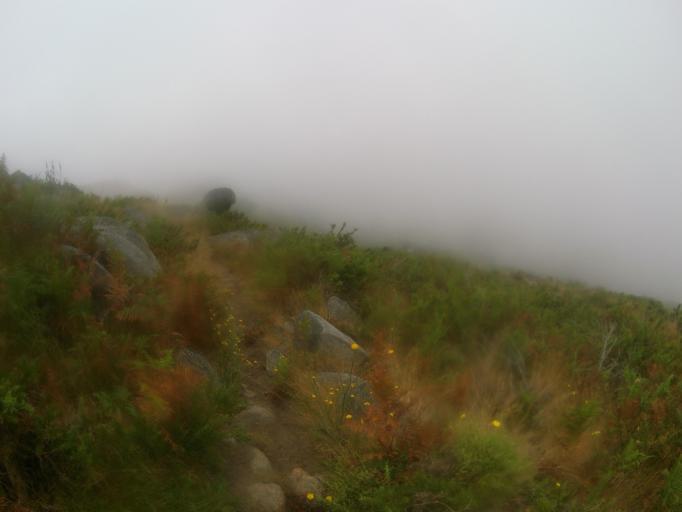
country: PT
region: Viana do Castelo
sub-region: Ponte de Lima
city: Ponte de Lima
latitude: 41.7123
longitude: -8.6000
